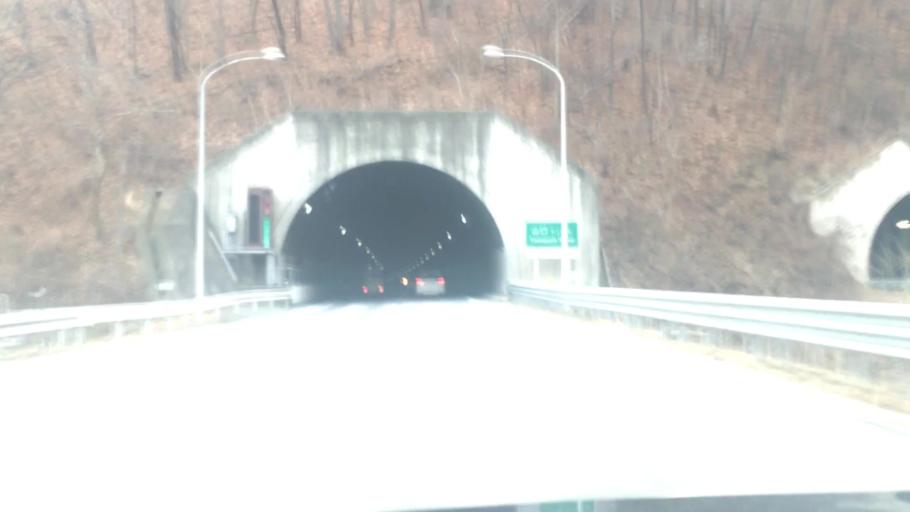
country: JP
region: Nagano
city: Ueda
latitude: 36.4212
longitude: 138.2718
